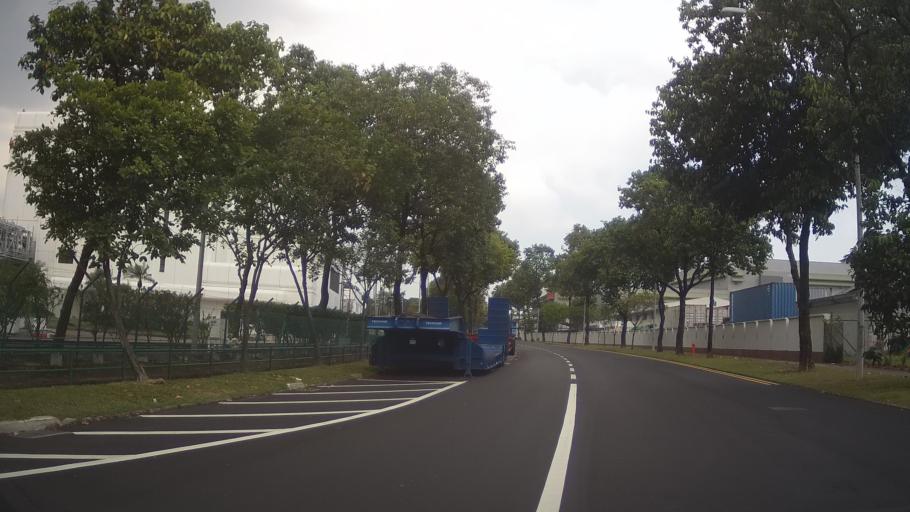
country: MY
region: Johor
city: Johor Bahru
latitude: 1.3069
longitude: 103.6612
